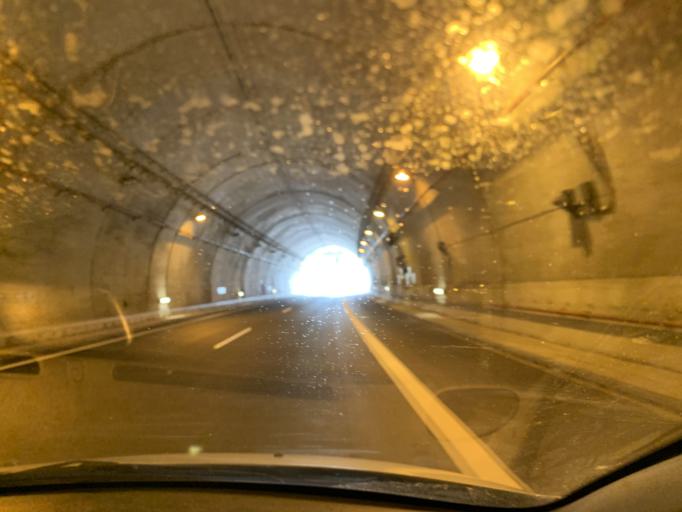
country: ES
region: Asturias
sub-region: Province of Asturias
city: Cudillero
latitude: 43.5431
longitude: -6.1537
